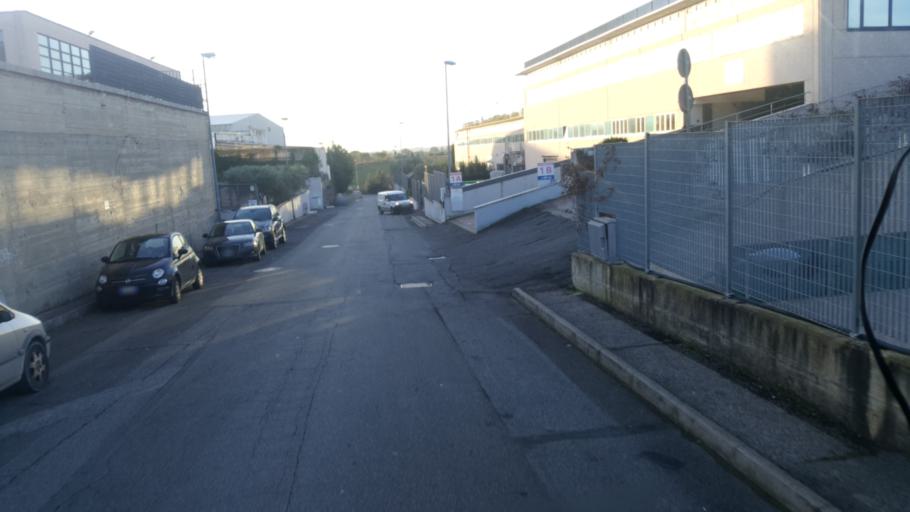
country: IT
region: Latium
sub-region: Citta metropolitana di Roma Capitale
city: Formello
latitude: 42.0509
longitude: 12.4030
